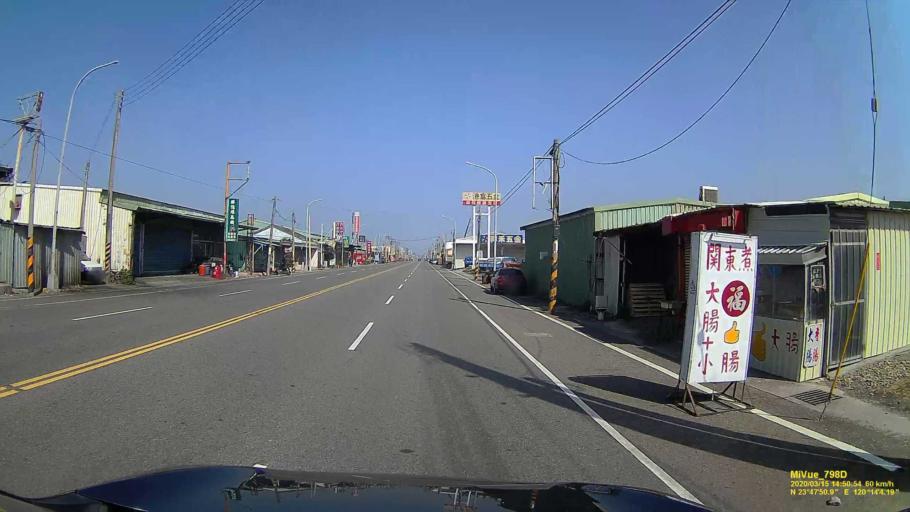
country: TW
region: Taiwan
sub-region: Yunlin
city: Douliu
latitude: 23.7975
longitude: 120.2347
